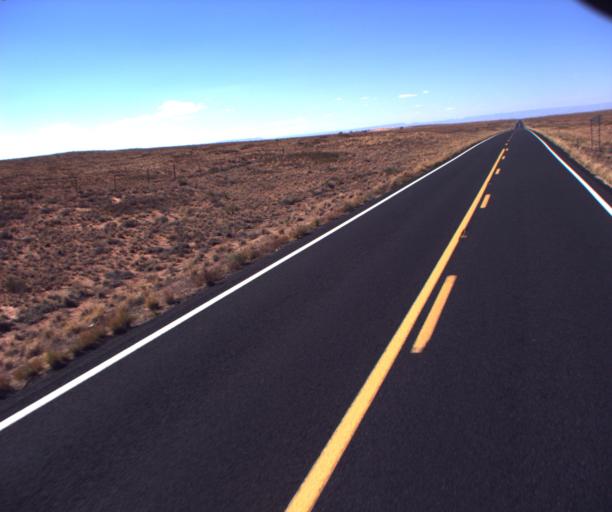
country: US
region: Arizona
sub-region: Coconino County
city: Tuba City
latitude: 36.0161
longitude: -111.0972
